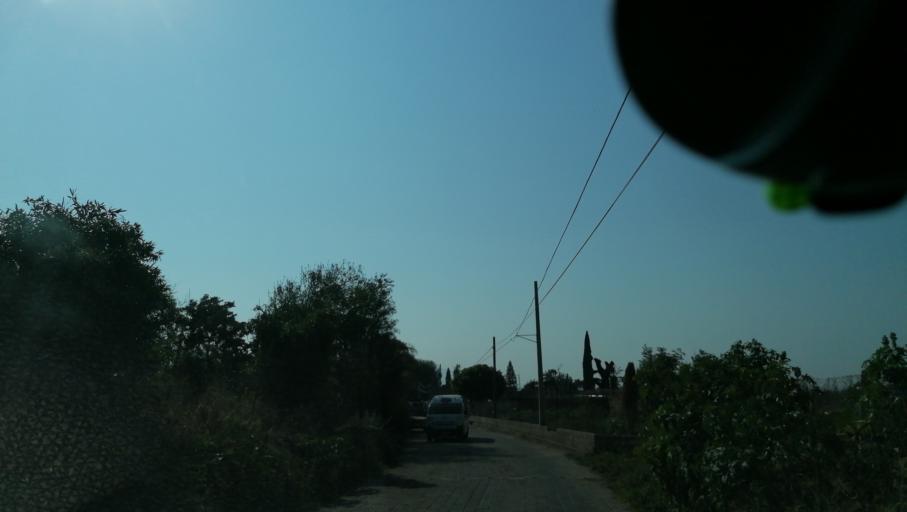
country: MX
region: Puebla
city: Atlixco
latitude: 18.9270
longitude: -98.4554
